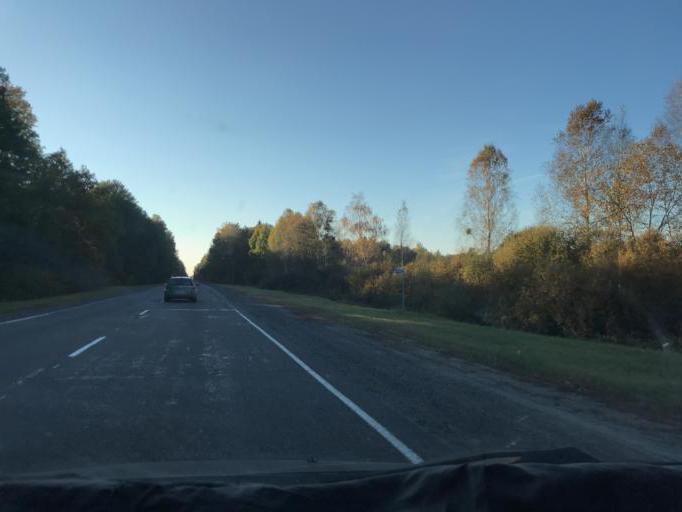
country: BY
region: Gomel
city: Pyetrykaw
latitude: 52.2747
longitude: 28.2432
